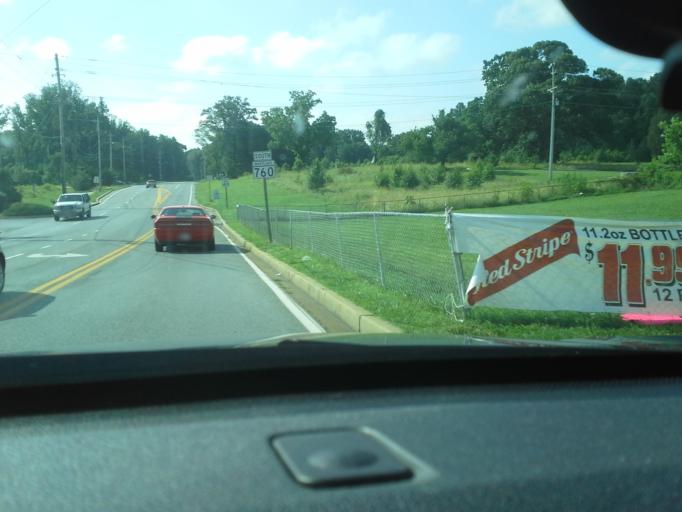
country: US
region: Maryland
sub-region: Calvert County
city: Chesapeake Ranch Estates
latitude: 38.3722
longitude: -76.4414
